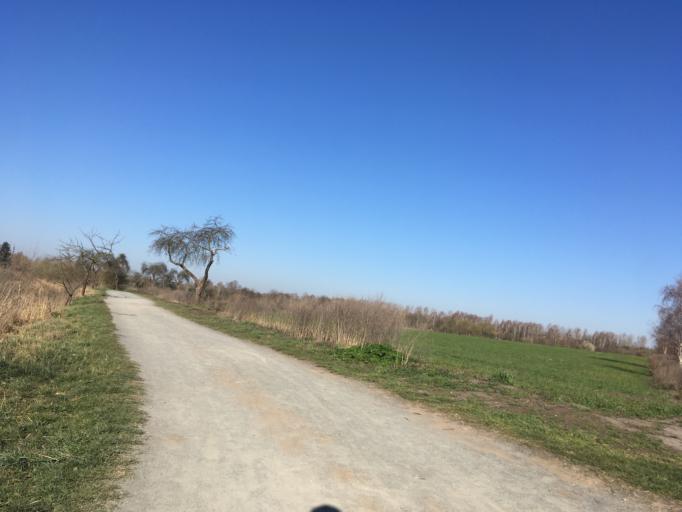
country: DE
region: Berlin
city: Blankenfelde
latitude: 52.6239
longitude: 13.4128
